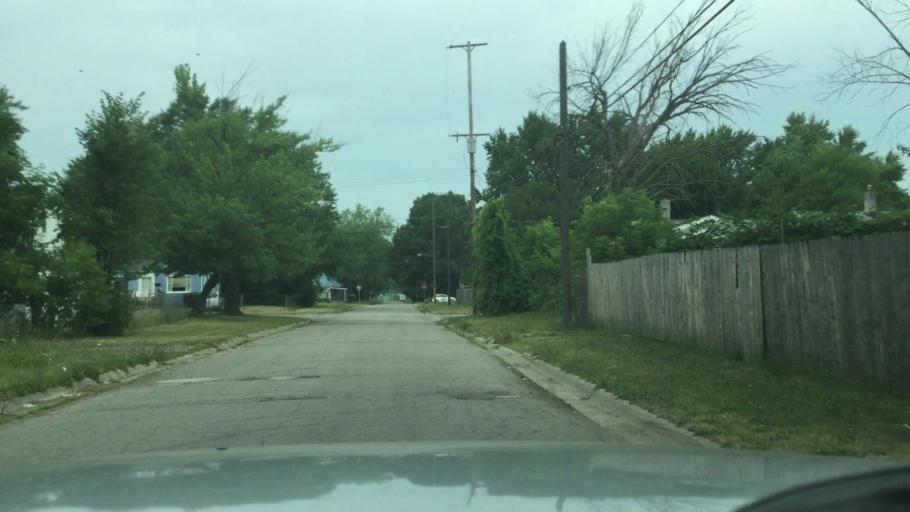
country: US
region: Michigan
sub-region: Genesee County
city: Flint
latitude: 42.9924
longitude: -83.6857
